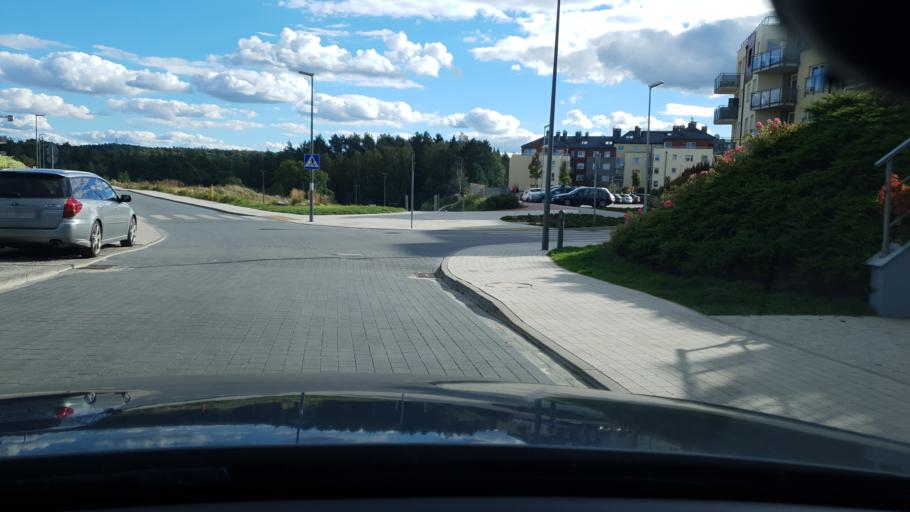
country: PL
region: Pomeranian Voivodeship
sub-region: Gdynia
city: Wielki Kack
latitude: 54.4944
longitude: 18.4414
